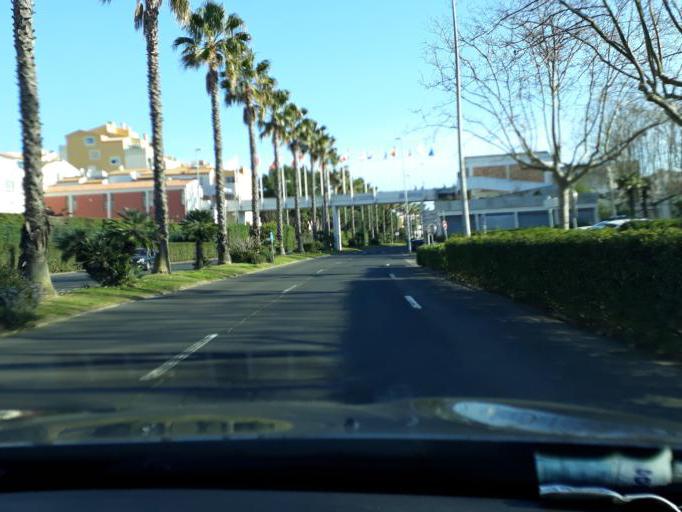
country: FR
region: Languedoc-Roussillon
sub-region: Departement de l'Herault
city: Le Cap d'Agde
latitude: 43.2847
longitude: 3.5146
